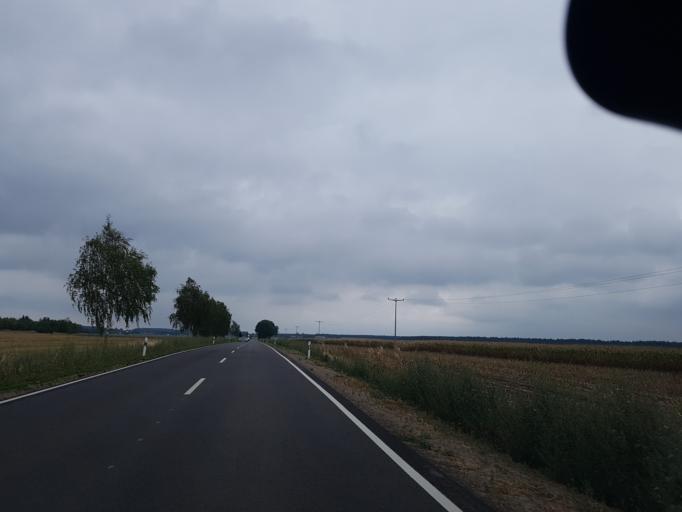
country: DE
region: Saxony-Anhalt
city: Tucheim
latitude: 52.2152
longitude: 12.1371
